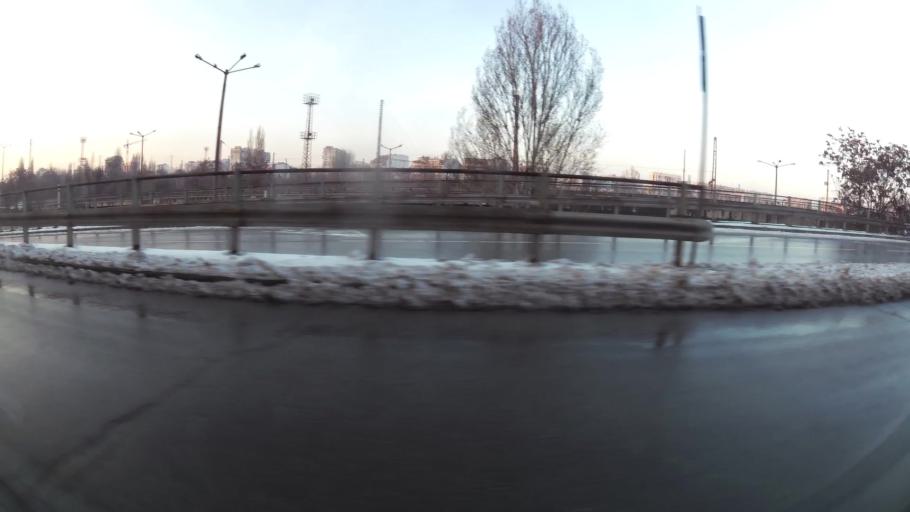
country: BG
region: Sofia-Capital
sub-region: Stolichna Obshtina
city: Sofia
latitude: 42.6966
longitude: 23.3588
